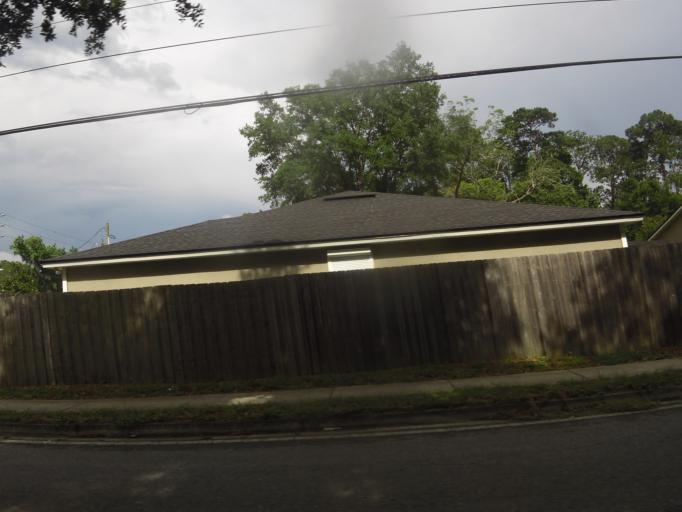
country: US
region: Florida
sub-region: Duval County
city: Jacksonville
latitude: 30.2894
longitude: -81.6102
